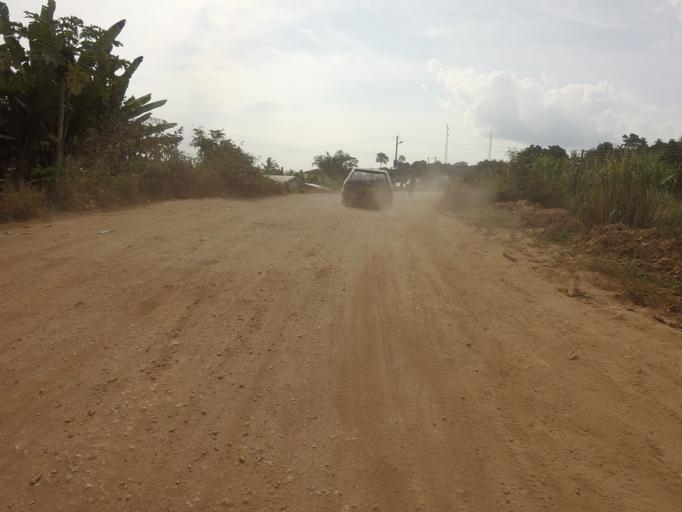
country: GH
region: Volta
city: Ho
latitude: 6.6833
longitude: 0.3350
